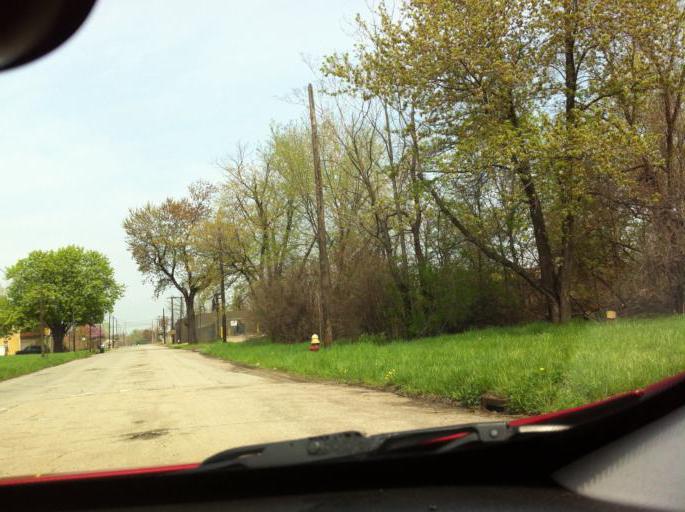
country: US
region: Michigan
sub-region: Wayne County
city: River Rouge
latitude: 42.3034
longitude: -83.0979
